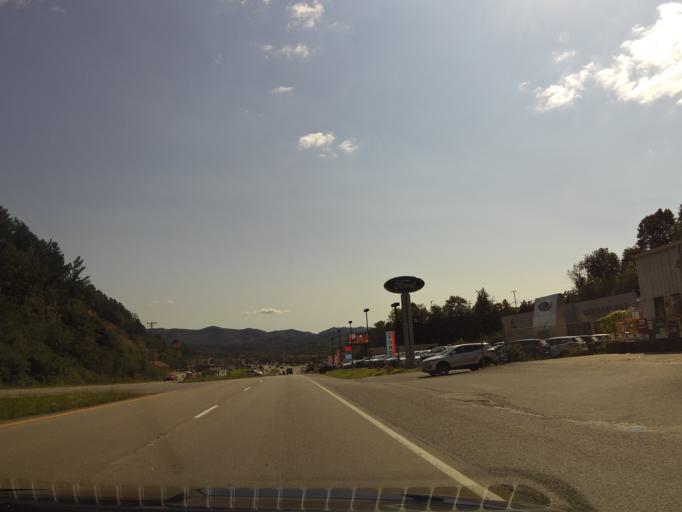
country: US
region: Kentucky
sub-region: Bell County
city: Middlesboro
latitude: 36.6274
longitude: -83.7038
